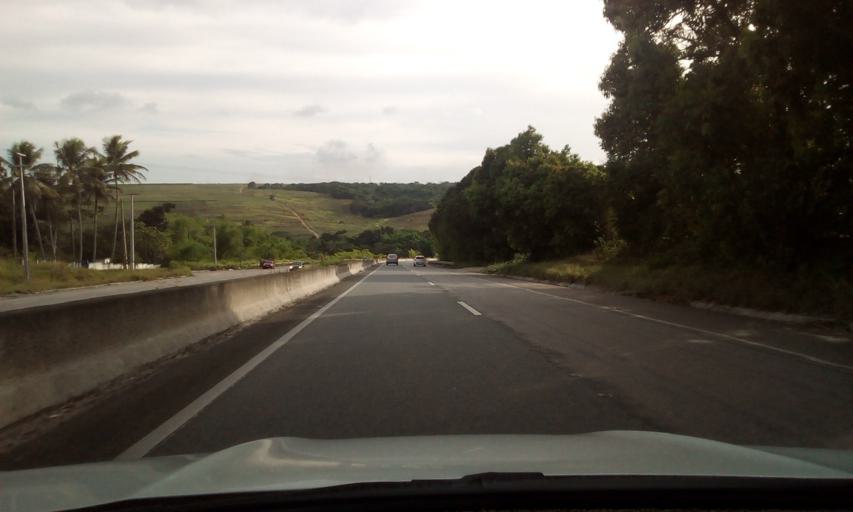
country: BR
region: Paraiba
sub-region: Alhandra
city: Alhandra
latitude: -7.4315
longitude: -34.9682
